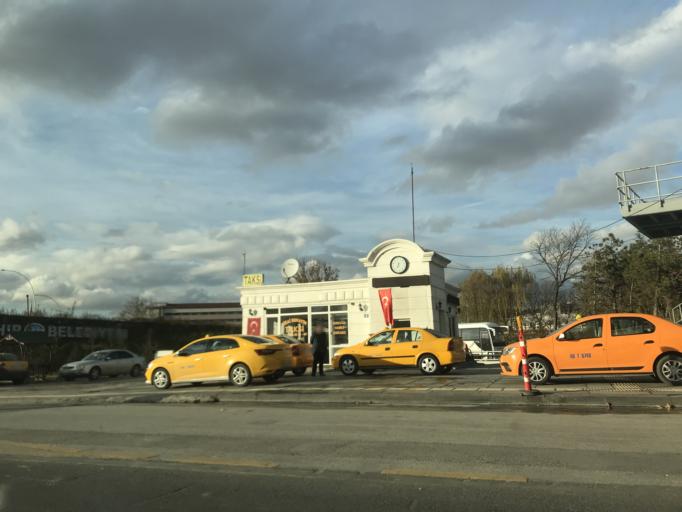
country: TR
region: Ankara
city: Ankara
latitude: 39.9591
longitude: 32.8608
